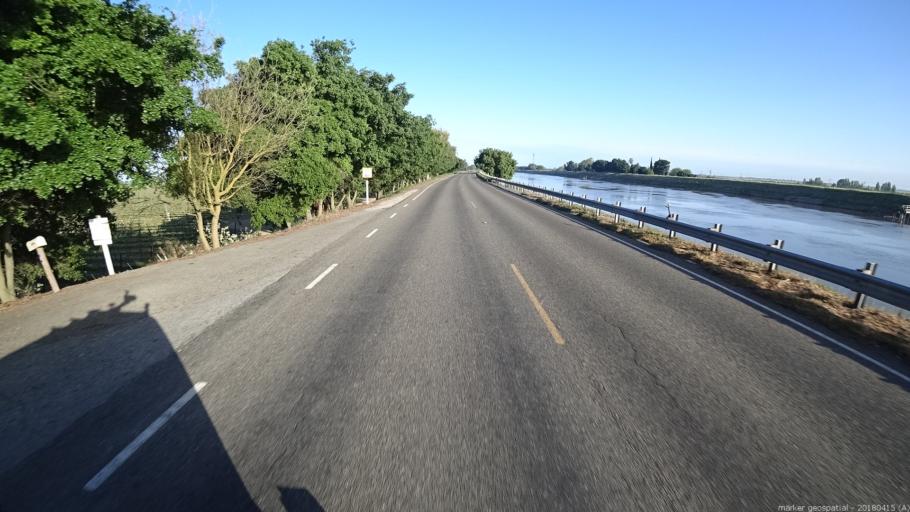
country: US
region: California
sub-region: Sacramento County
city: Walnut Grove
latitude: 38.2852
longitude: -121.5554
